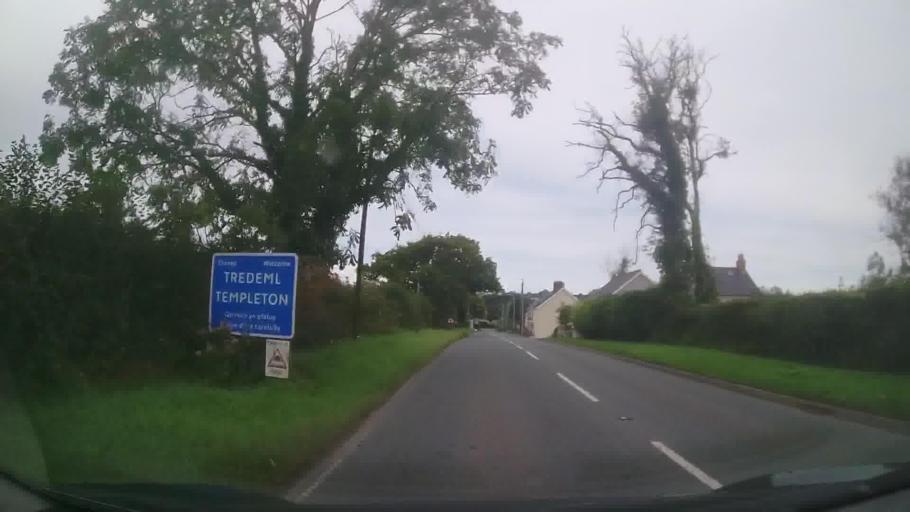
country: GB
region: Wales
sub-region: Pembrokeshire
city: Templeton
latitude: 51.7656
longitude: -4.7368
